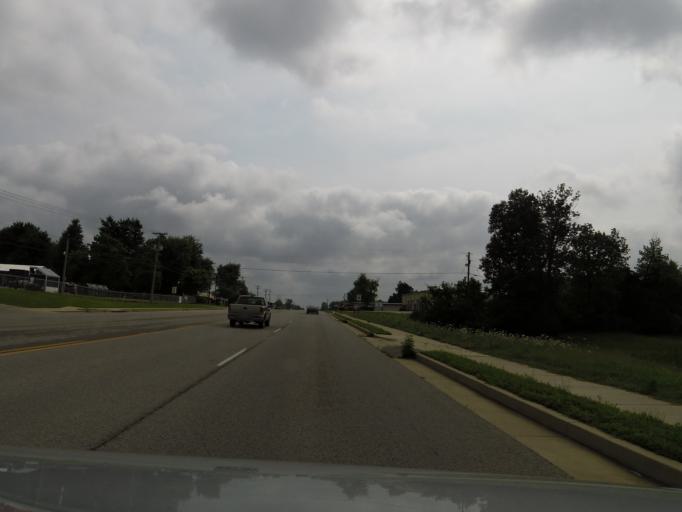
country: US
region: Kentucky
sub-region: Hopkins County
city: Madisonville
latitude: 37.3263
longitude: -87.4527
